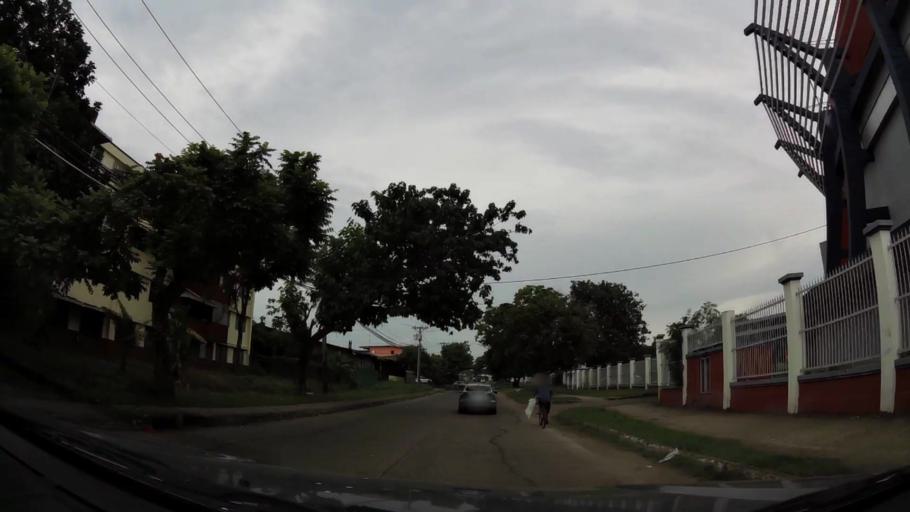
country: PA
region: Panama
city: San Miguelito
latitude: 9.0327
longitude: -79.4715
